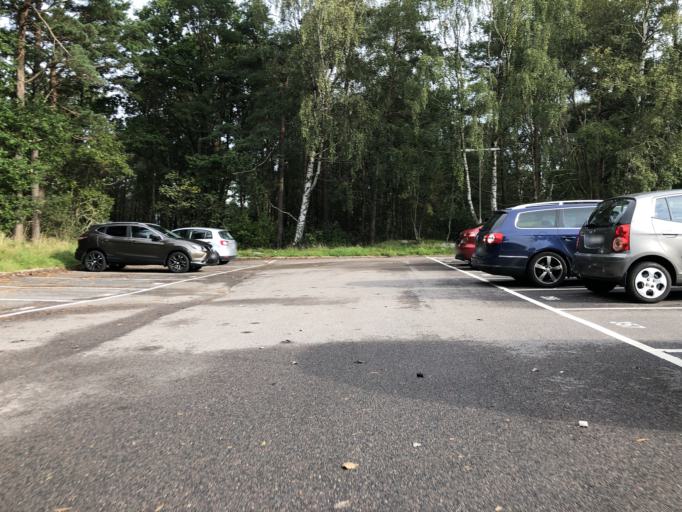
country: SE
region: Vaestra Goetaland
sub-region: Goteborg
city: Majorna
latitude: 57.7380
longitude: 11.8924
